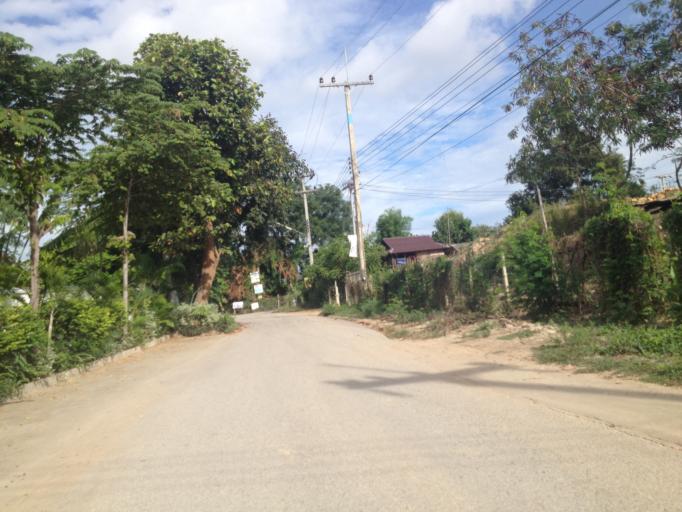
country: TH
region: Chiang Mai
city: Hang Dong
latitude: 18.6986
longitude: 98.8959
